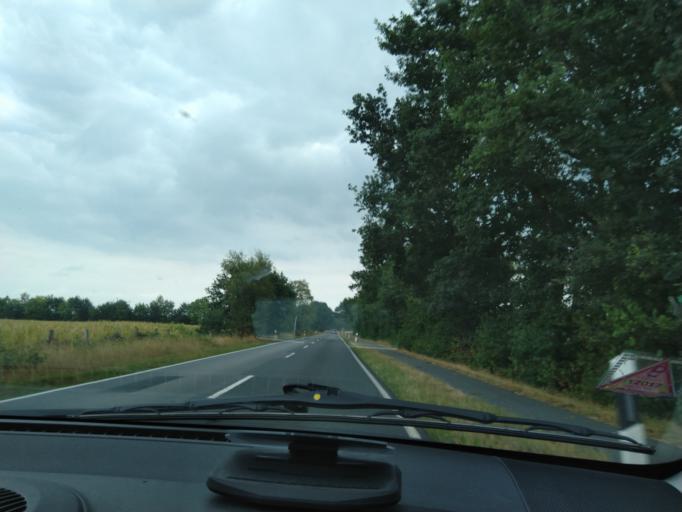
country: DE
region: Lower Saxony
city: Rhede
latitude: 53.0687
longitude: 7.2113
